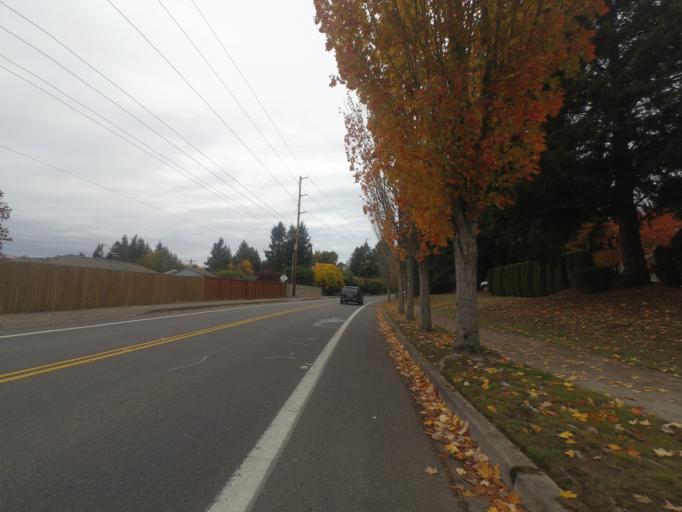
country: US
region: Washington
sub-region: Pierce County
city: University Place
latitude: 47.2167
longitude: -122.5663
